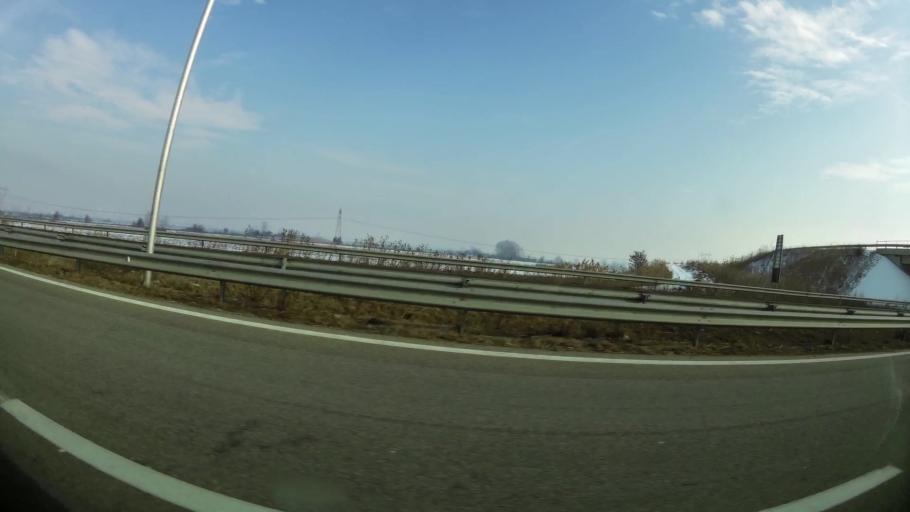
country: MK
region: Aracinovo
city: Arachinovo
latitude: 42.0078
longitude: 21.5350
